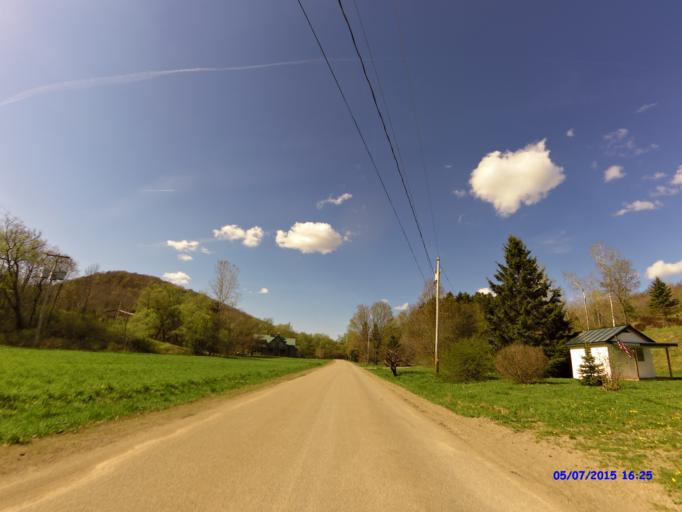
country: US
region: New York
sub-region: Cattaraugus County
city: Little Valley
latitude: 42.2900
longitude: -78.6781
